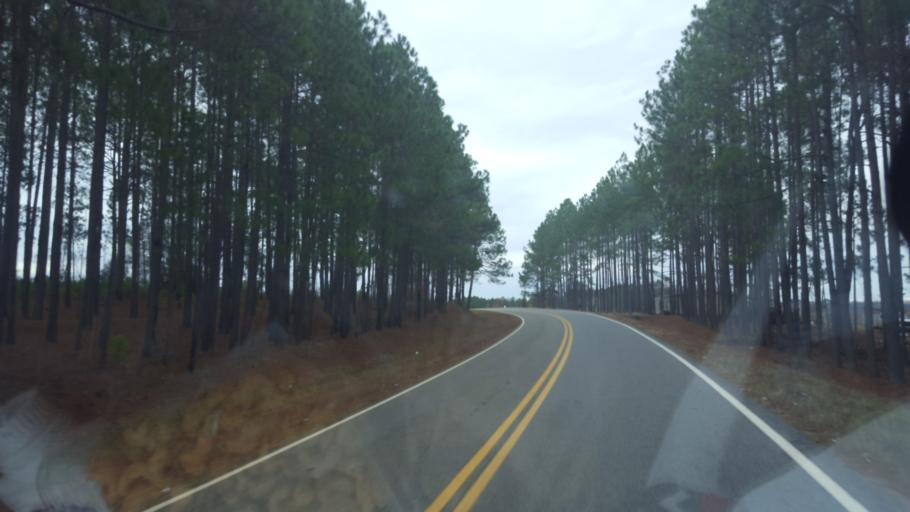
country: US
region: Georgia
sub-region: Wilcox County
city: Rochelle
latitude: 31.7840
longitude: -83.4332
